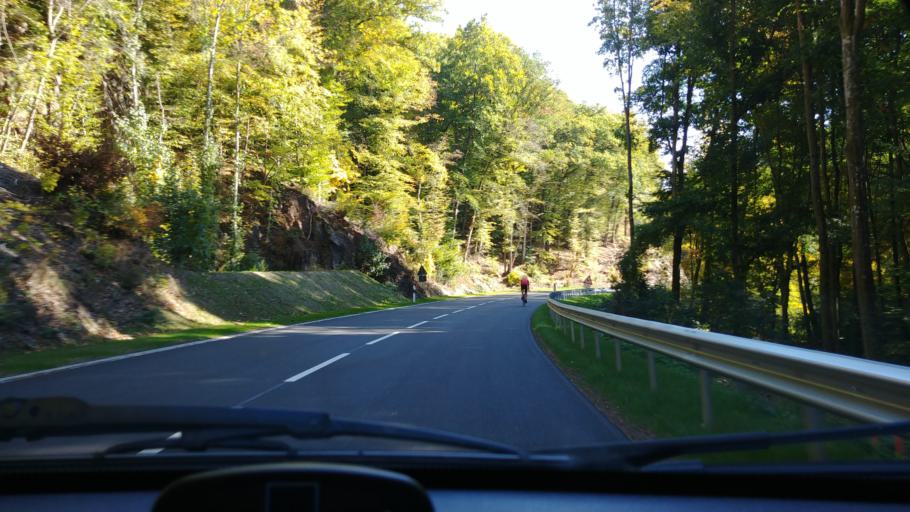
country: DE
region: Rheinland-Pfalz
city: Mudershausen
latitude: 50.2868
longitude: 8.0469
